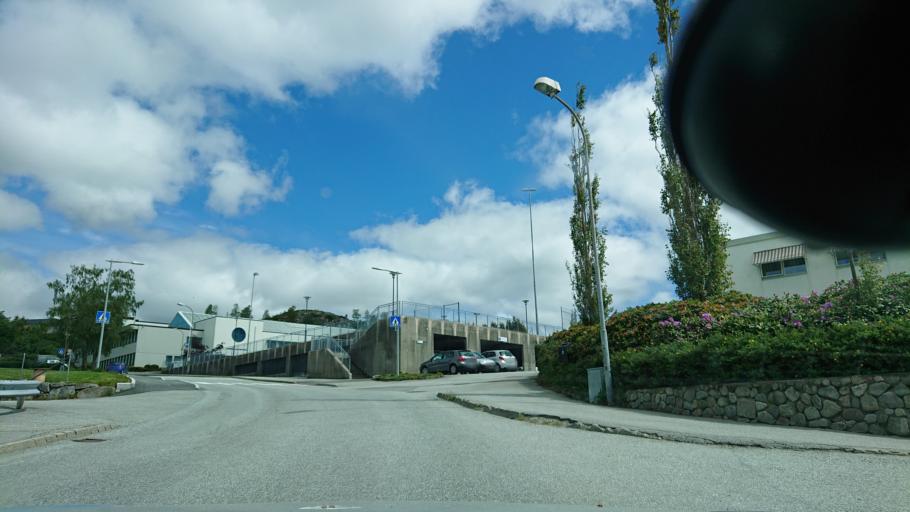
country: NO
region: Rogaland
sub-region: Gjesdal
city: Algard
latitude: 58.7677
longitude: 5.8655
